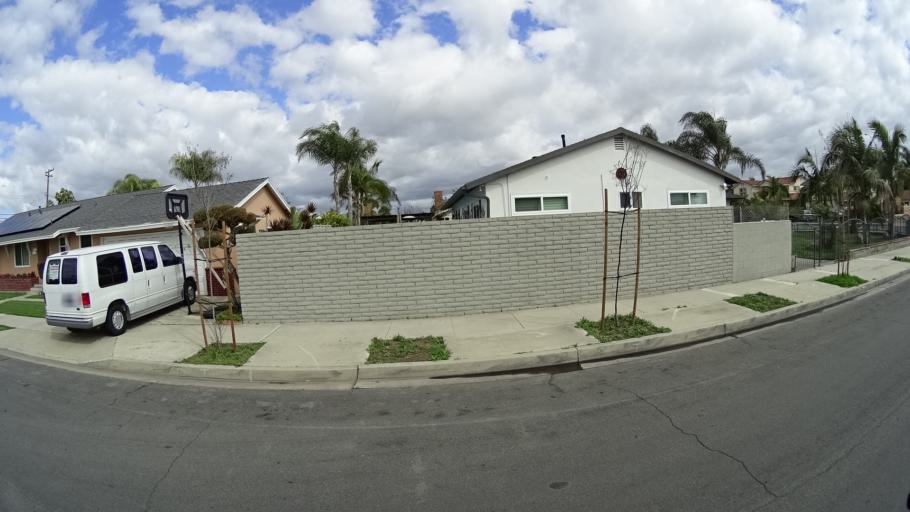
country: US
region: California
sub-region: Orange County
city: Anaheim
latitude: 33.8293
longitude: -117.9545
